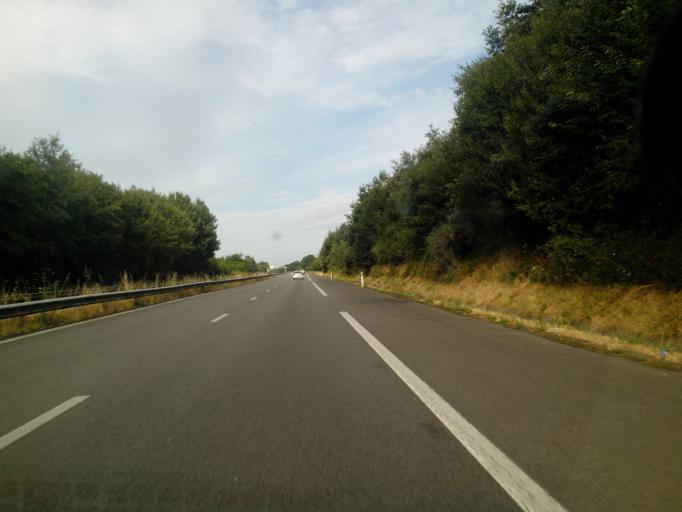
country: FR
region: Pays de la Loire
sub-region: Departement de la Loire-Atlantique
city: Orvault
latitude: 47.2572
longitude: -1.6355
